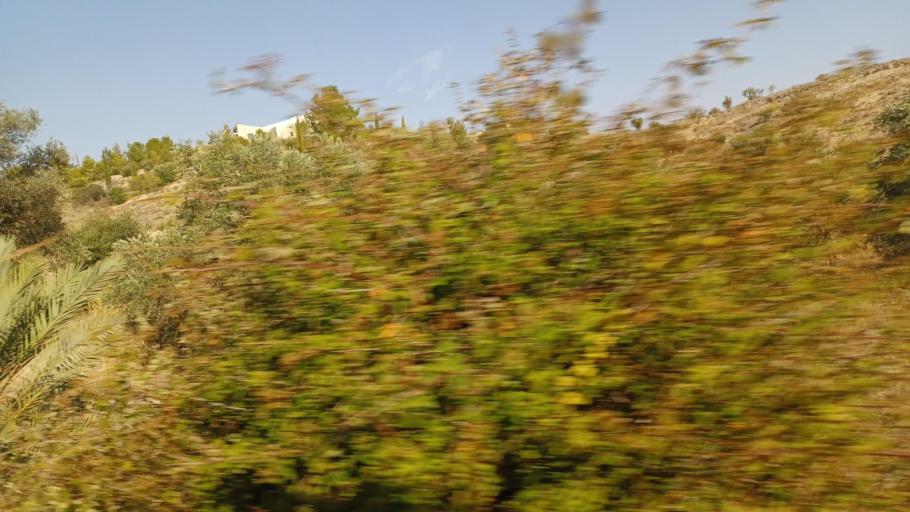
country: CY
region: Lefkosia
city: Alampra
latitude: 34.9836
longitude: 33.3561
